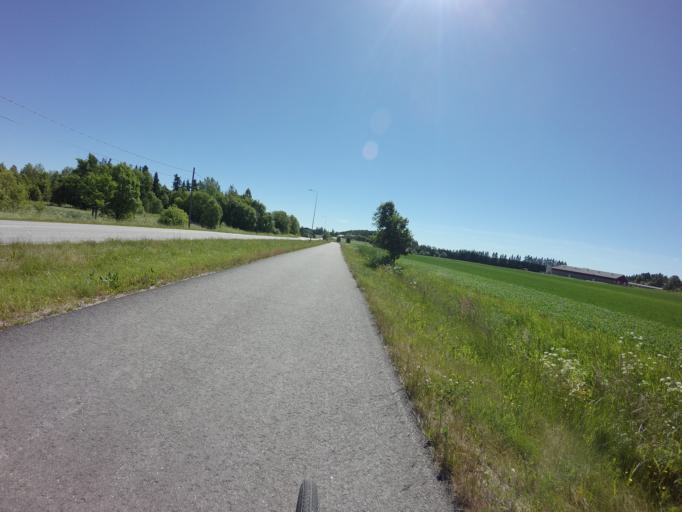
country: FI
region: Varsinais-Suomi
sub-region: Turku
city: Turku
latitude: 60.4982
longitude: 22.3312
